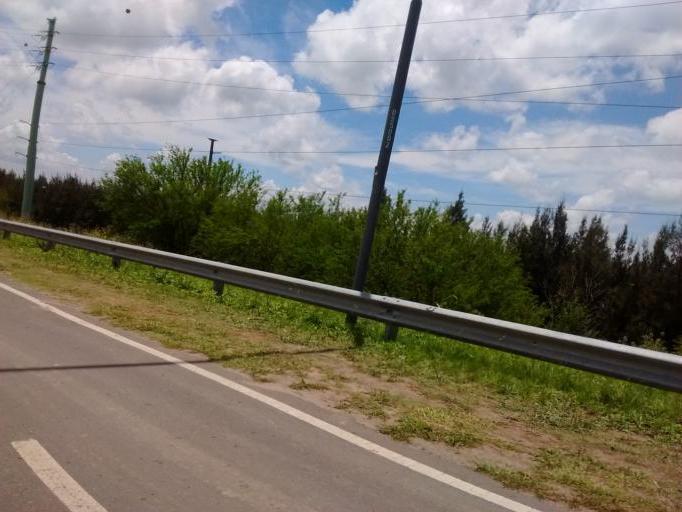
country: AR
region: Santa Fe
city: Funes
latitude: -32.9214
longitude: -60.7770
